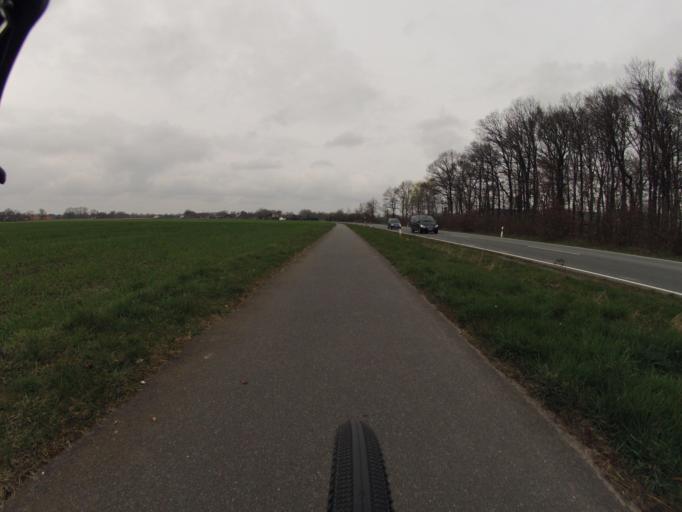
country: DE
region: North Rhine-Westphalia
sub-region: Regierungsbezirk Munster
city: Recke
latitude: 52.3461
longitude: 7.7330
